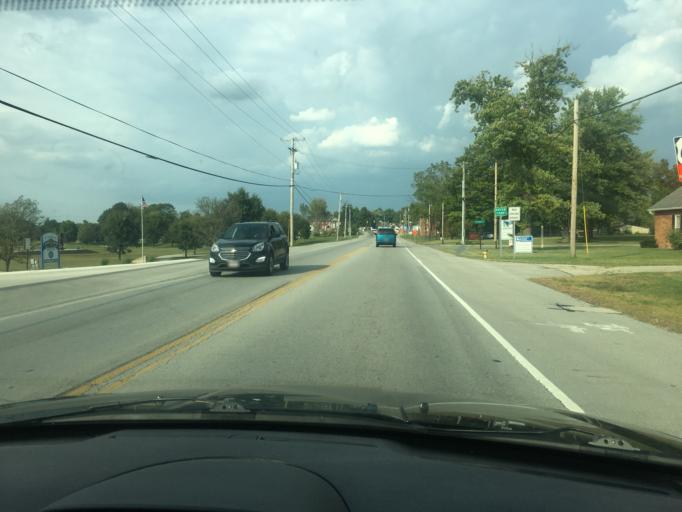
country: US
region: Ohio
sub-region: Champaign County
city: Urbana
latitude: 40.0906
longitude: -83.7562
